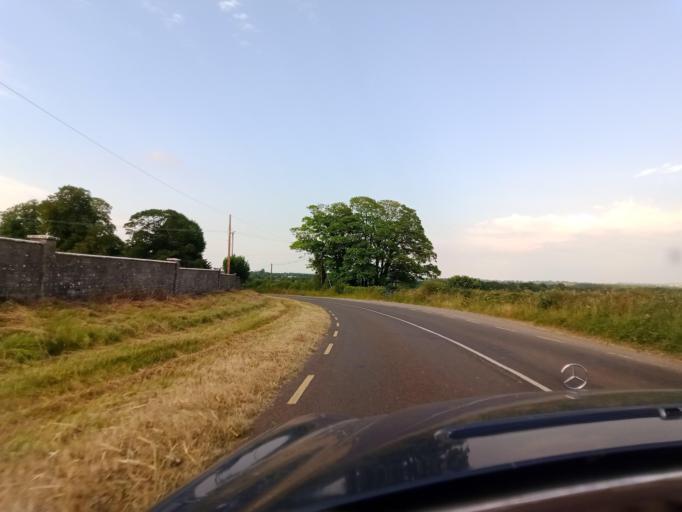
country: IE
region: Leinster
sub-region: Kilkenny
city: Callan
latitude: 52.4853
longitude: -7.3240
